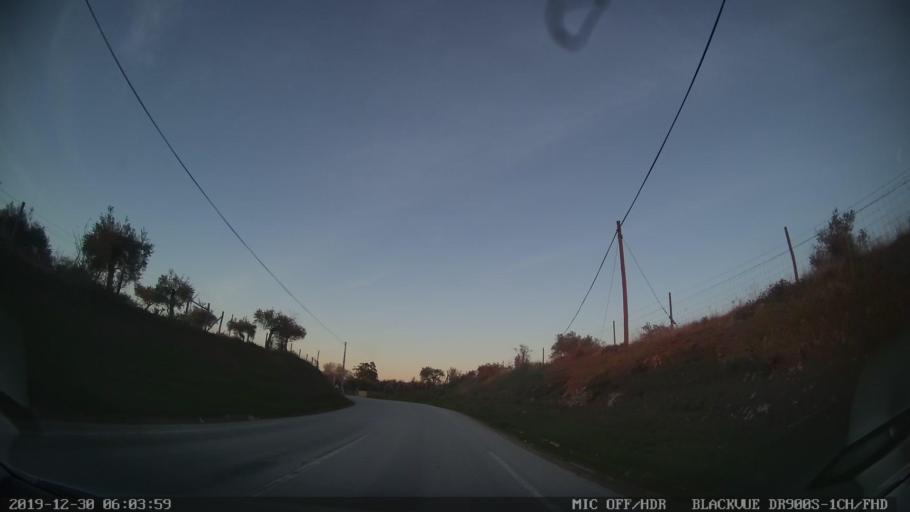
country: PT
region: Castelo Branco
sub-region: Penamacor
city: Penamacor
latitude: 40.0810
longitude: -7.2403
